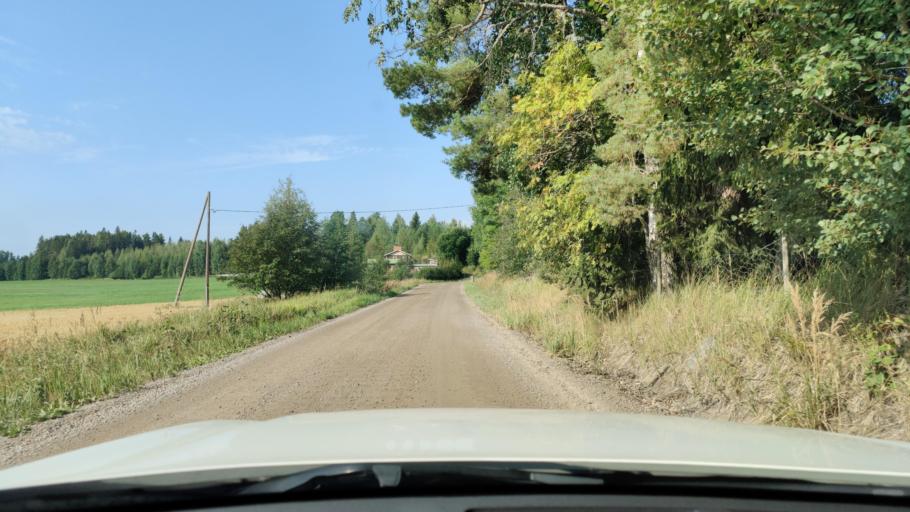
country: FI
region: Haeme
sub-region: Riihimaeki
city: Loppi
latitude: 60.6758
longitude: 24.5786
